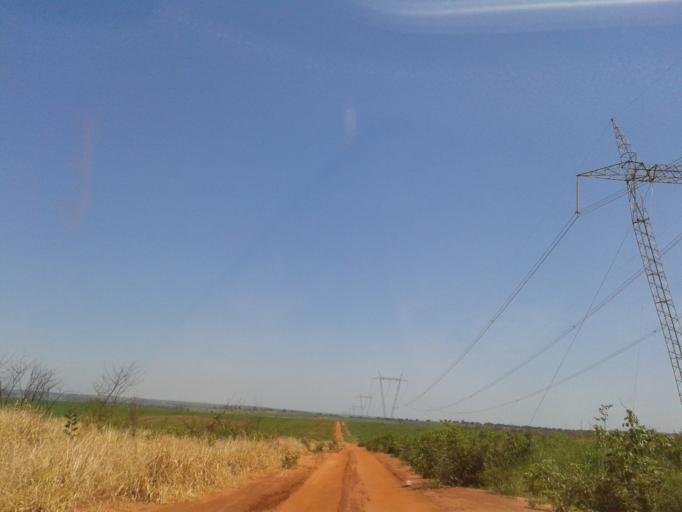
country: BR
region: Minas Gerais
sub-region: Santa Vitoria
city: Santa Vitoria
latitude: -19.0781
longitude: -50.4584
